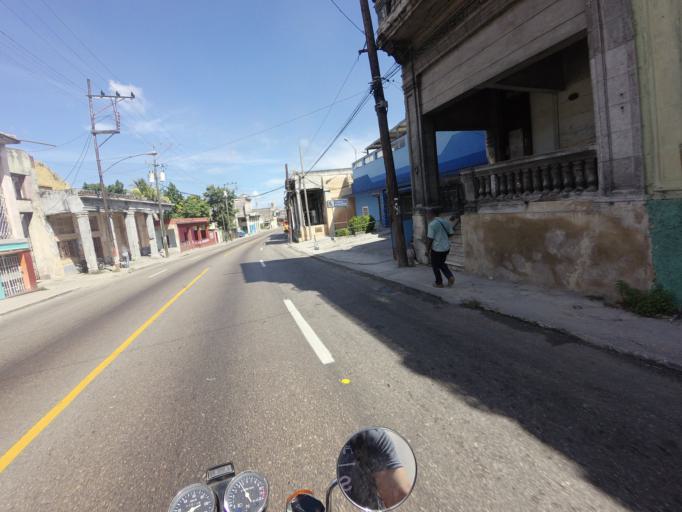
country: CU
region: La Habana
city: Diez de Octubre
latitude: 23.0999
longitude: -82.3626
